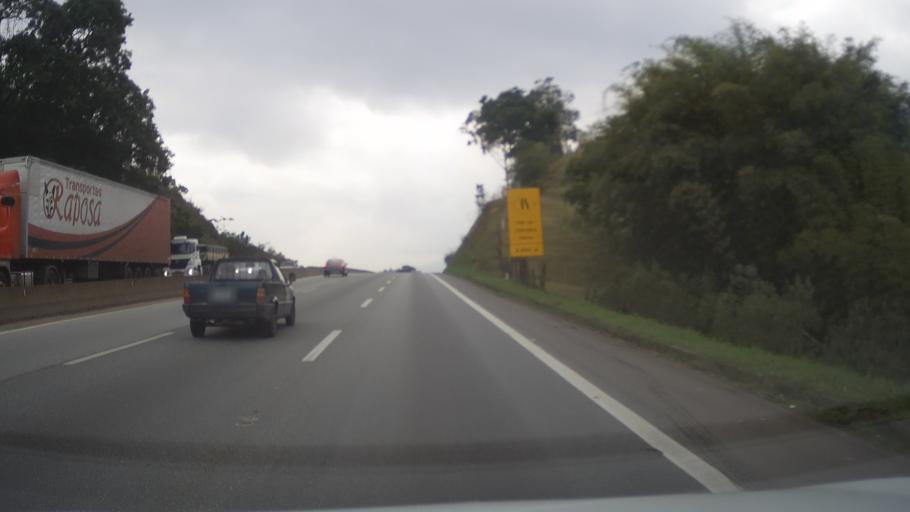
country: BR
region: Minas Gerais
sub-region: Extrema
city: Extrema
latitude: -22.8681
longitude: -46.3540
